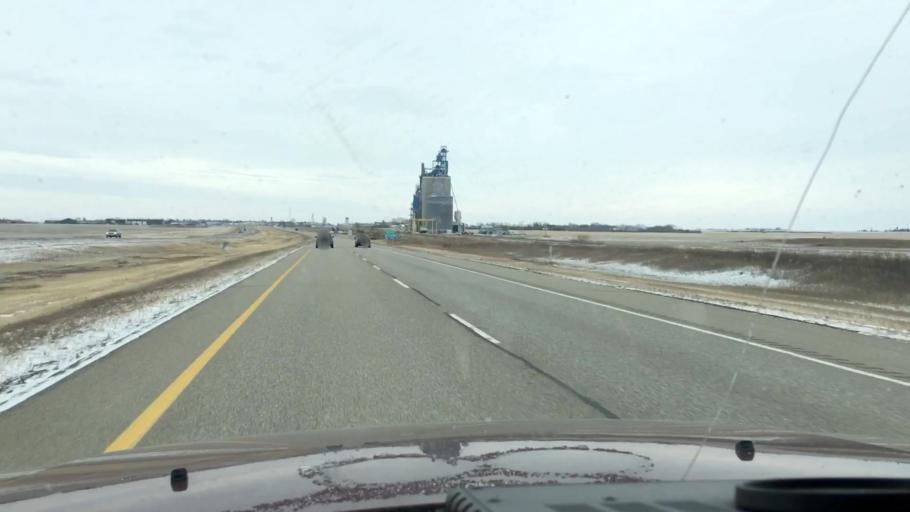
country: CA
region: Saskatchewan
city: Watrous
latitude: 51.2845
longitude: -106.0211
